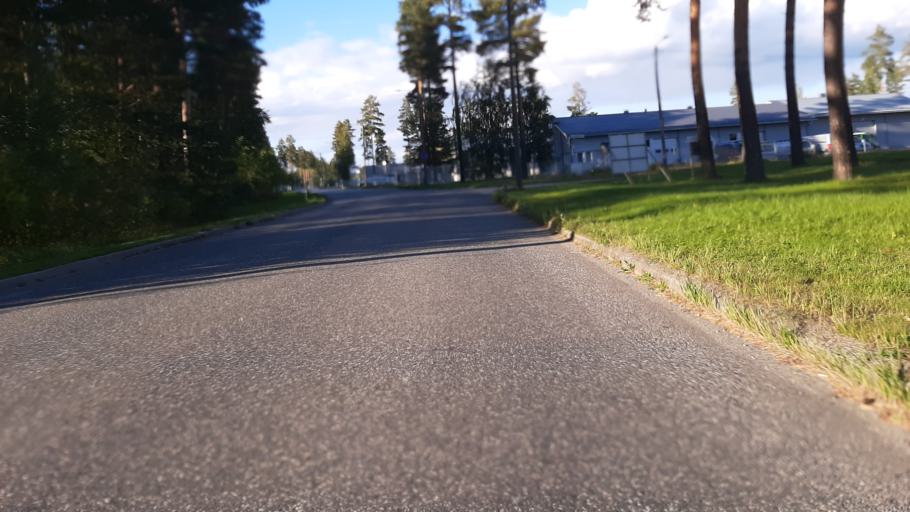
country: FI
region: North Karelia
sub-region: Joensuu
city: Joensuu
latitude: 62.6253
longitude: 29.7710
